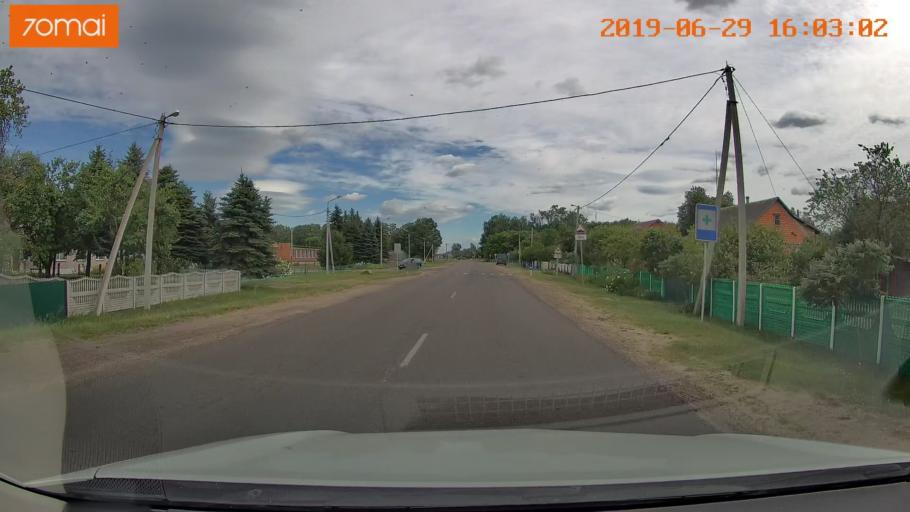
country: BY
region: Brest
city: Luninyets
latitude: 52.2313
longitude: 27.0173
